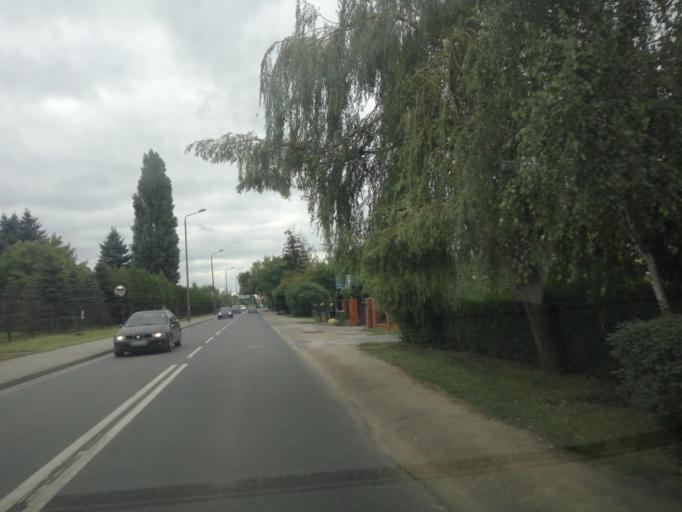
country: PL
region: Lower Silesian Voivodeship
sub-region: Powiat wroclawski
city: Zerniki Wroclawskie
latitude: 51.0559
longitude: 17.0323
